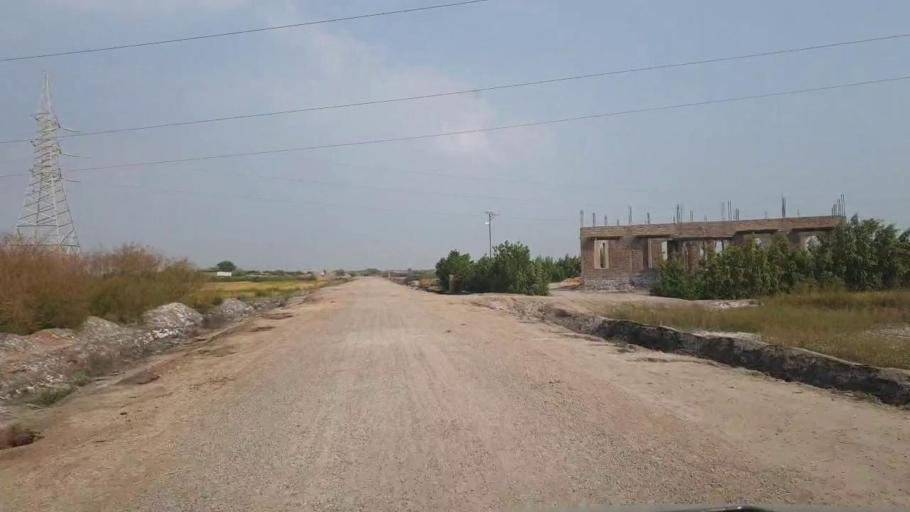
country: PK
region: Sindh
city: Matli
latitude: 24.9605
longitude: 68.6863
